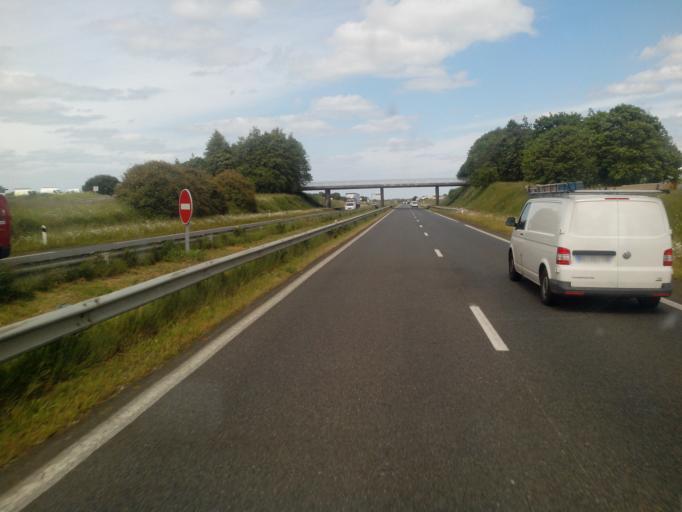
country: FR
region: Brittany
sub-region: Departement des Cotes-d'Armor
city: Tremuson
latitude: 48.5293
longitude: -2.8595
